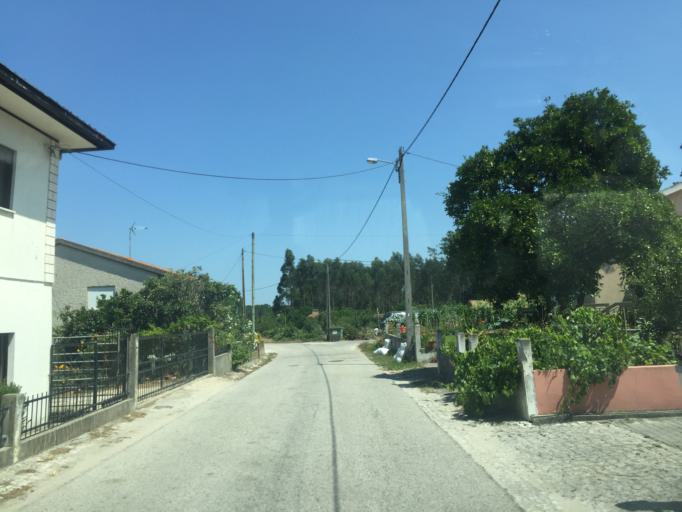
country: PT
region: Coimbra
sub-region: Mira
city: Mira
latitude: 40.3388
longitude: -8.7295
